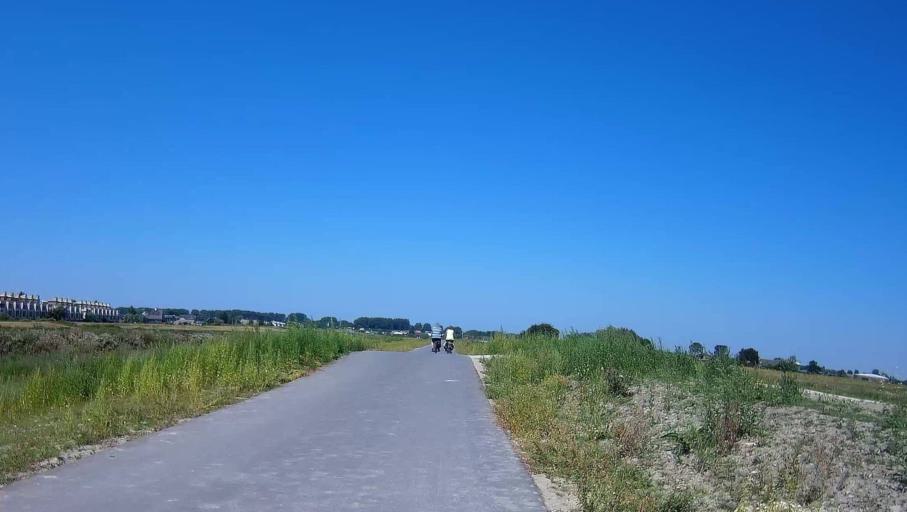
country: NL
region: South Holland
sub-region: Gemeente Pijnacker-Nootdorp
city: Pijnacker
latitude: 52.0692
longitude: 4.4169
